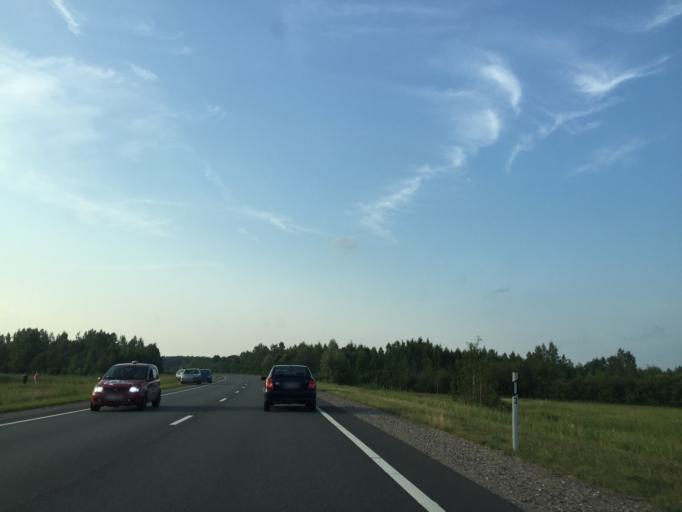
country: LV
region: Ozolnieku
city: Ozolnieki
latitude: 56.6705
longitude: 23.8238
